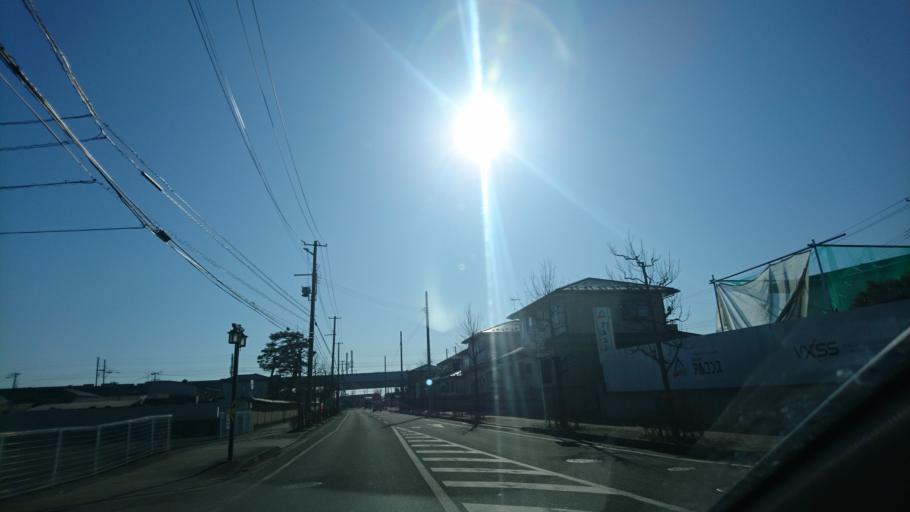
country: JP
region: Miyagi
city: Furukawa
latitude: 38.5873
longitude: 140.9704
